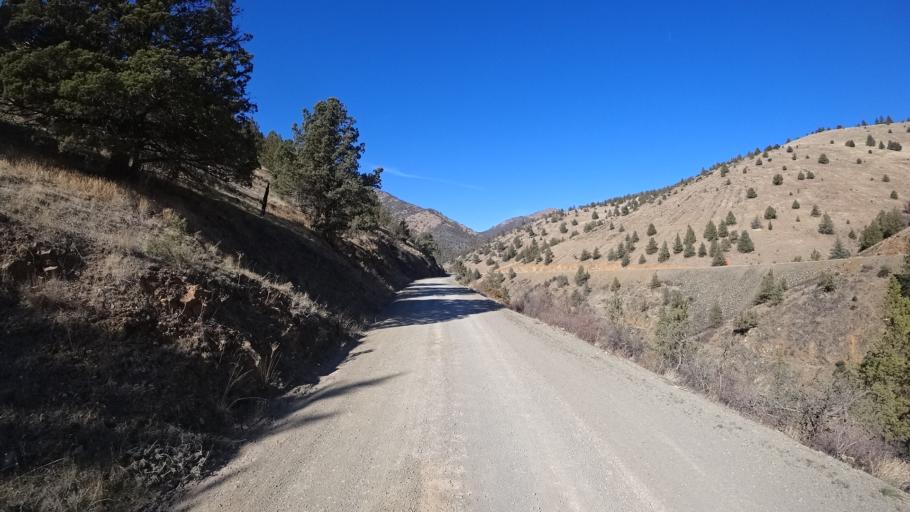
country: US
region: California
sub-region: Siskiyou County
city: Yreka
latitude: 41.7868
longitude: -122.6037
